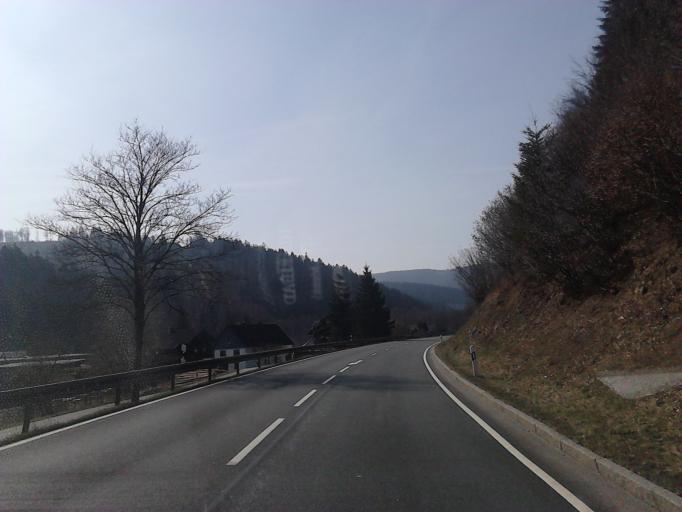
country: DE
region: Bavaria
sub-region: Upper Franconia
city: Wallenfels
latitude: 50.2667
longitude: 11.5080
